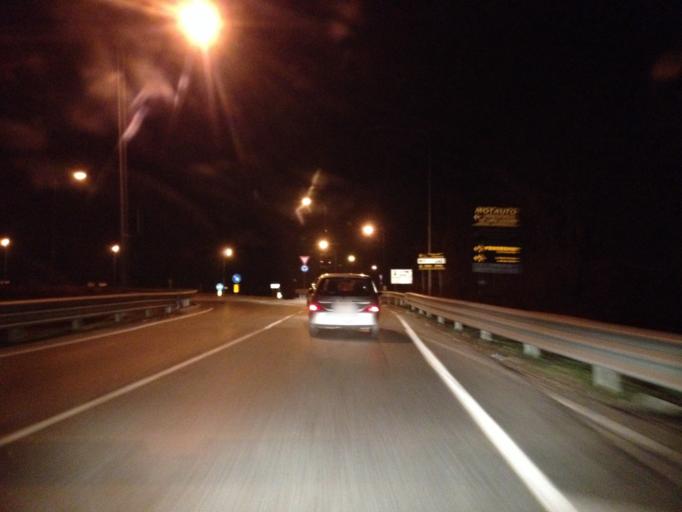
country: IT
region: Piedmont
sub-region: Provincia di Torino
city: Settimo Torinese
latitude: 45.1219
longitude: 7.7598
